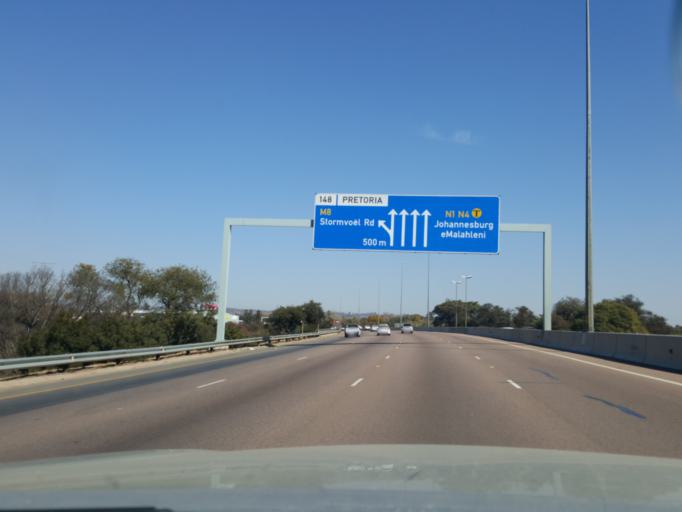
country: ZA
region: Gauteng
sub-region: City of Tshwane Metropolitan Municipality
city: Pretoria
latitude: -25.7031
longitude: 28.2713
